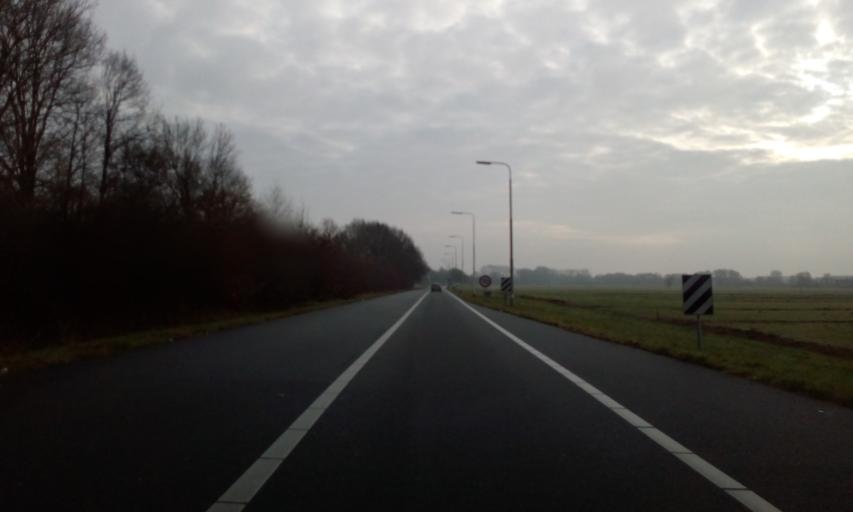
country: NL
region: North Holland
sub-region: Gemeente Naarden
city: Naarden
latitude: 52.3029
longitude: 5.1381
